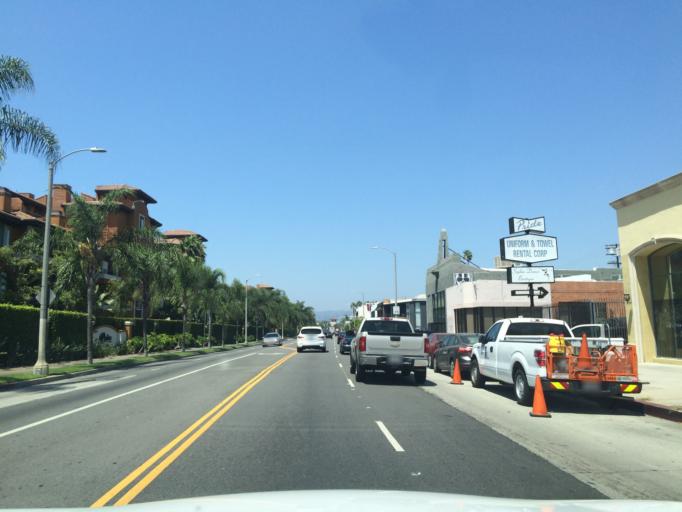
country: US
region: California
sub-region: Los Angeles County
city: West Hollywood
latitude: 34.0693
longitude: -118.3476
